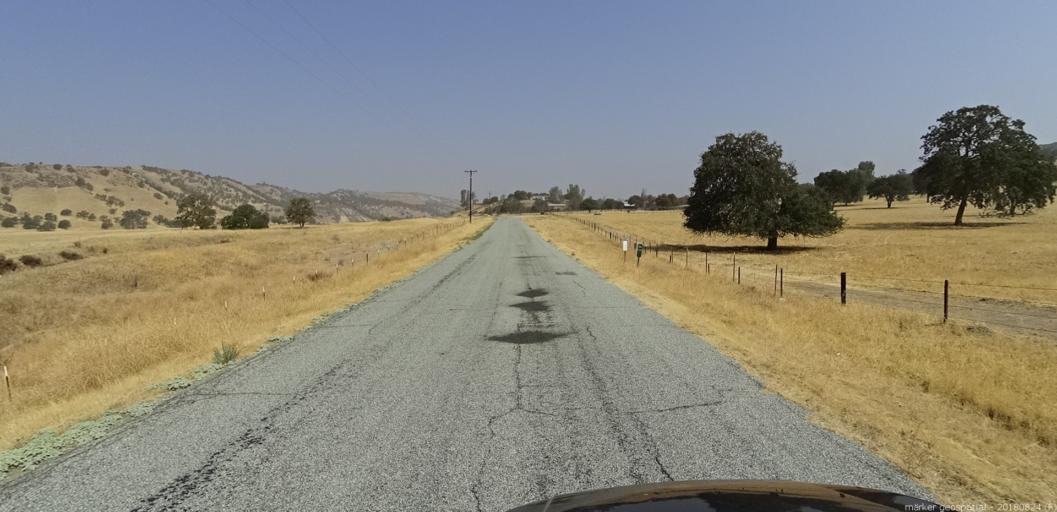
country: US
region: California
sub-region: San Luis Obispo County
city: San Miguel
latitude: 35.8507
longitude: -120.7000
